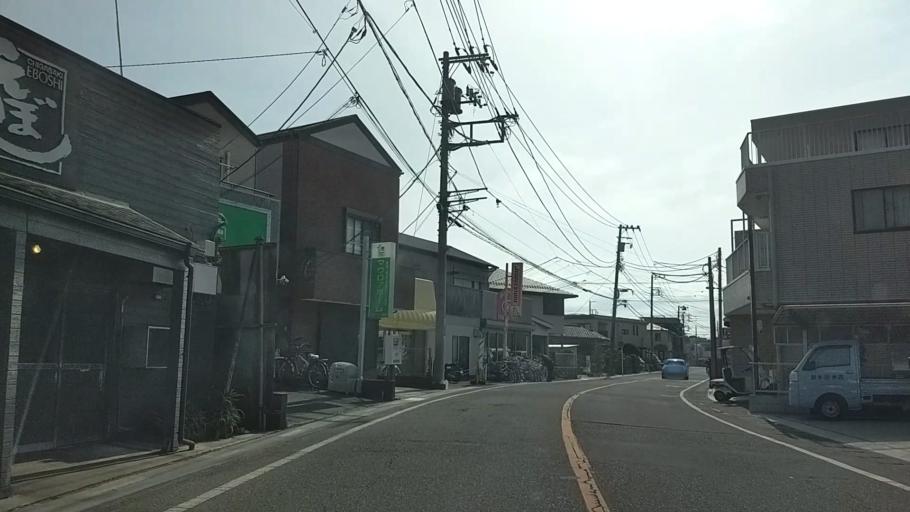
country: JP
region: Kanagawa
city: Chigasaki
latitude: 35.3222
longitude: 139.3884
